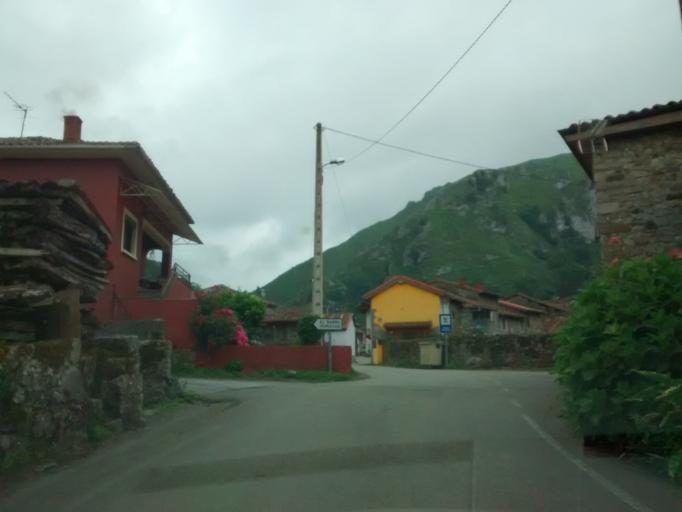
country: ES
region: Asturias
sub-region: Province of Asturias
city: Pilona
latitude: 43.3014
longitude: -5.3634
